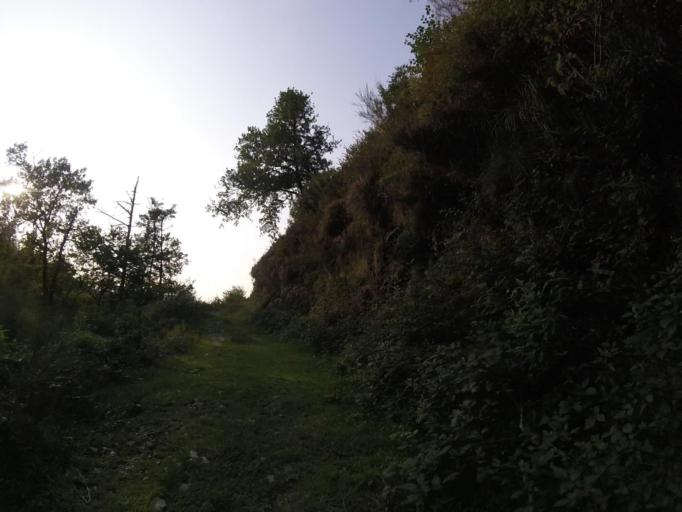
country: ES
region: Navarre
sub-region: Provincia de Navarra
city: Arano
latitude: 43.2527
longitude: -1.8382
